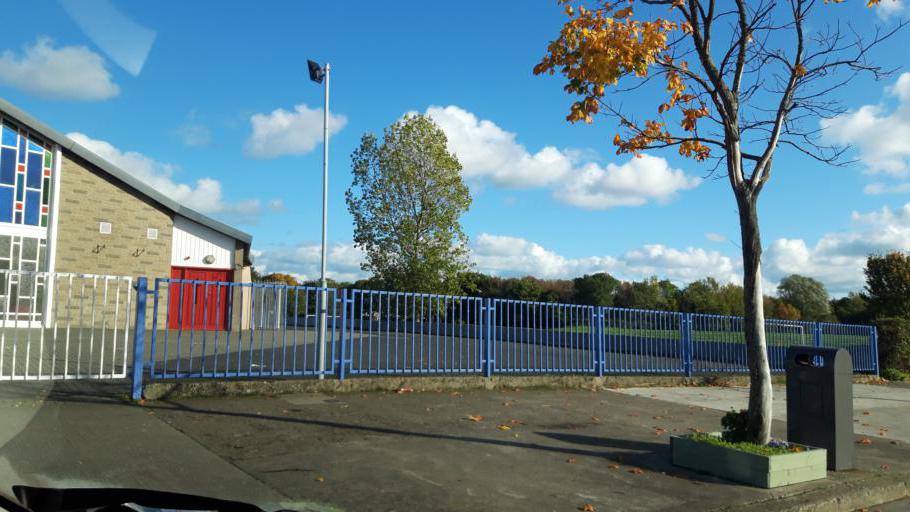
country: IE
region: Leinster
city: Raheny
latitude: 53.3875
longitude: -6.1813
